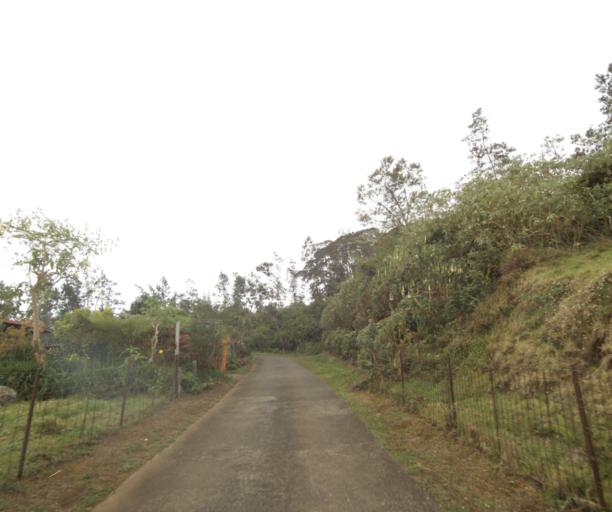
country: RE
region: Reunion
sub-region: Reunion
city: Saint-Paul
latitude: -21.0167
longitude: 55.3500
